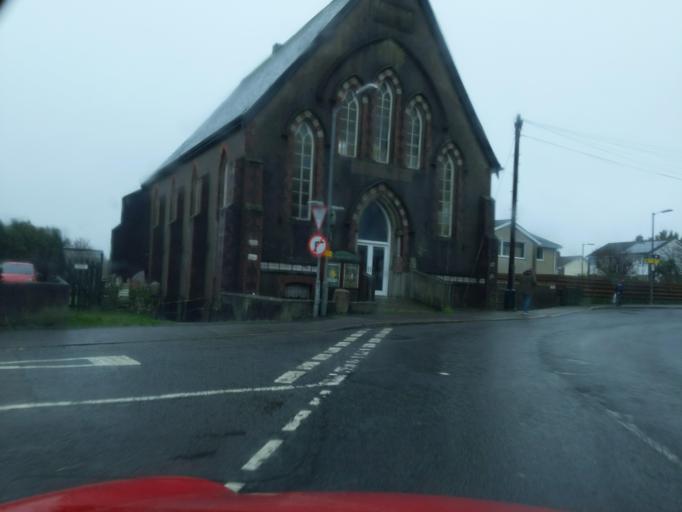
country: GB
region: England
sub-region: Cornwall
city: Callington
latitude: 50.5048
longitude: -4.3145
